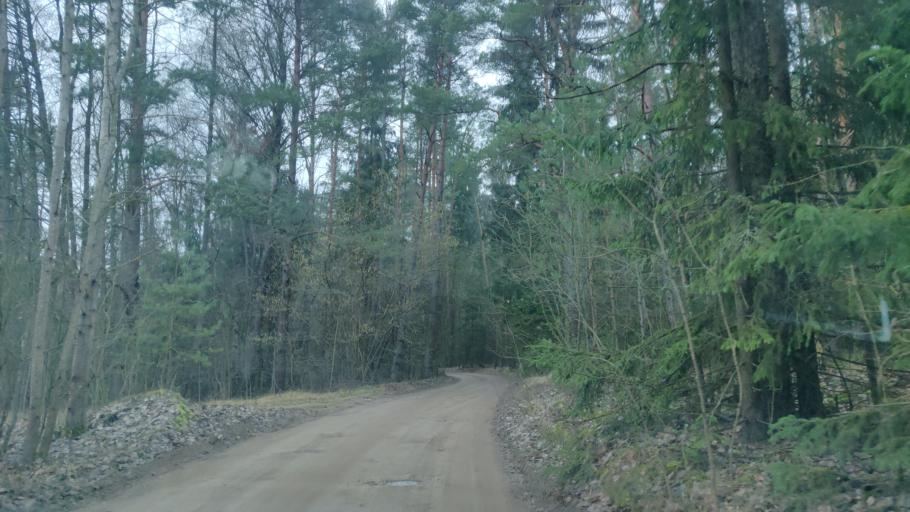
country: LT
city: Trakai
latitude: 54.5550
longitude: 24.9391
